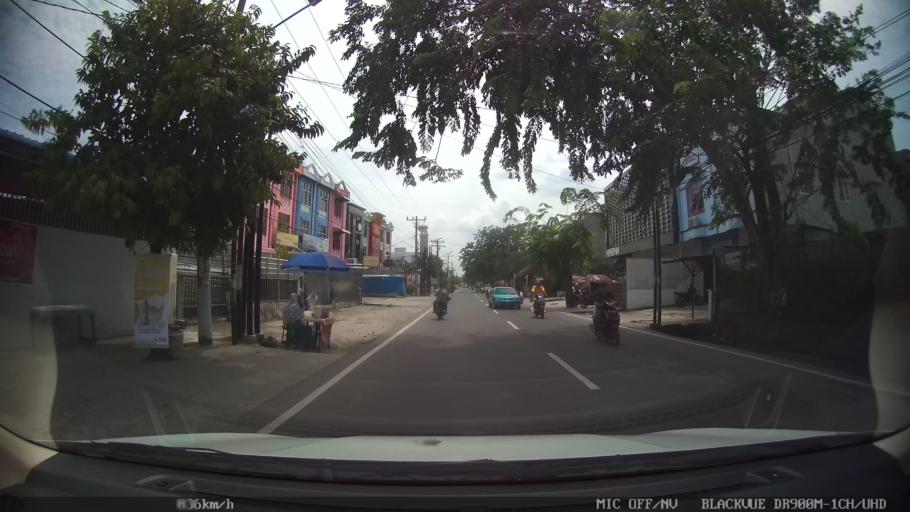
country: ID
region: North Sumatra
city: Sunggal
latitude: 3.5774
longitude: 98.6228
